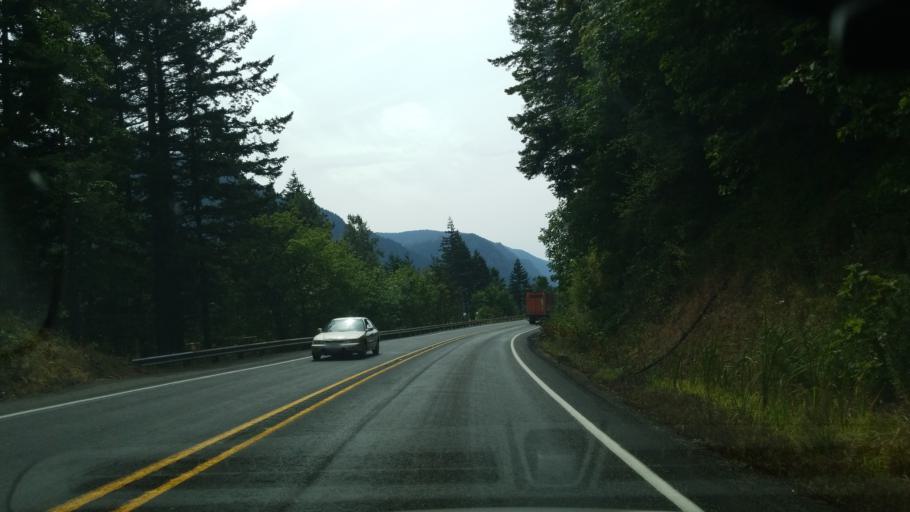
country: US
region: Oregon
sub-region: Hood River County
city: Cascade Locks
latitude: 45.6546
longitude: -121.9129
